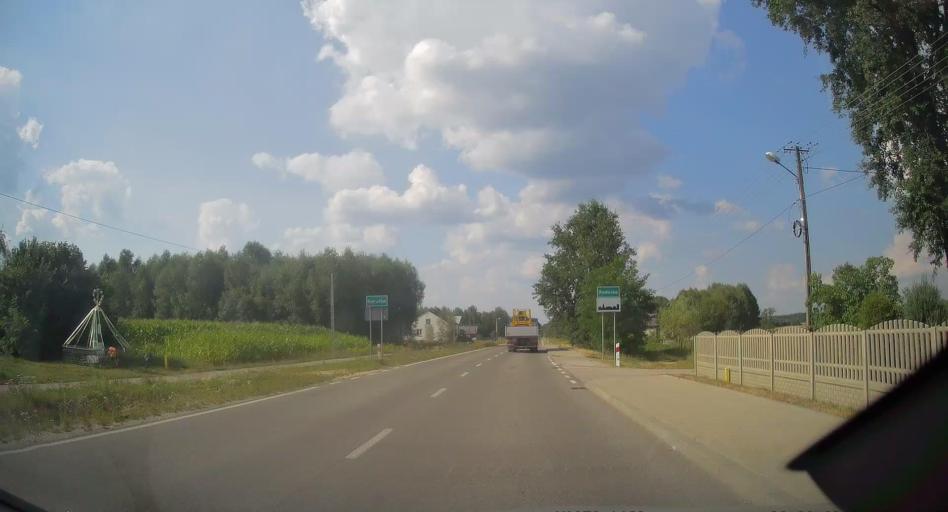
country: PL
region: Swietokrzyskie
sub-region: Powiat konecki
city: Radoszyce
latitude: 51.0550
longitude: 20.2794
